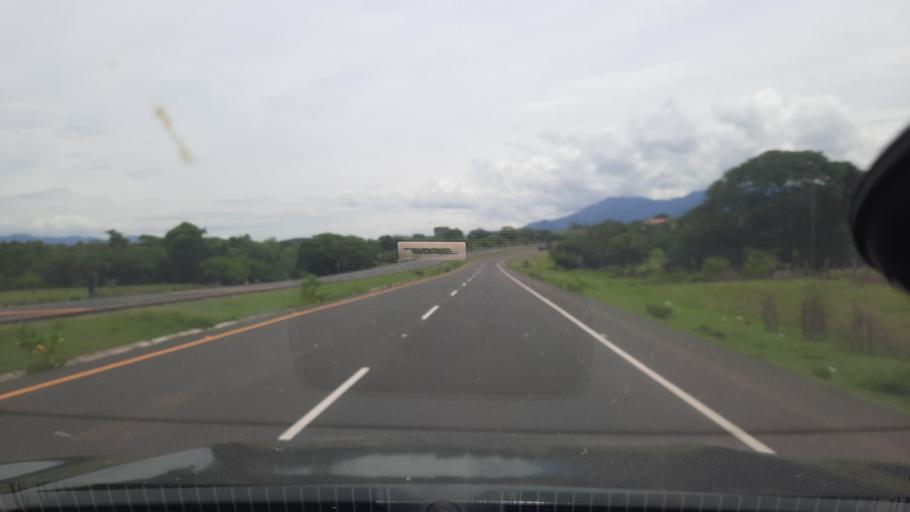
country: HN
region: Valle
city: Aramecina
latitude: 13.7004
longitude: -87.7148
